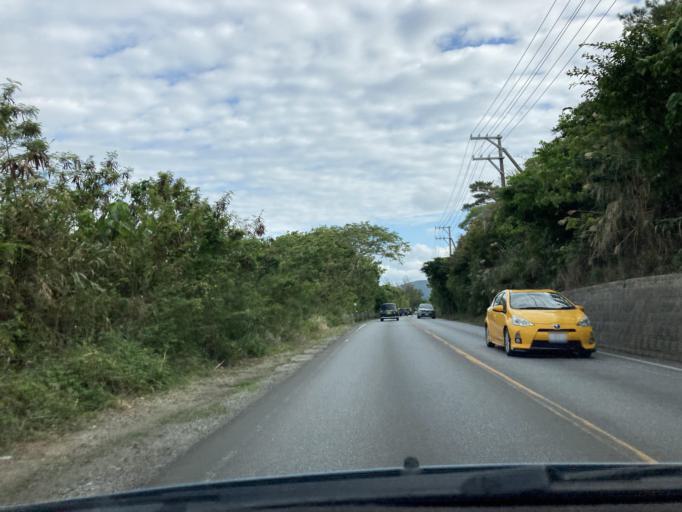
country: JP
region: Okinawa
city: Nago
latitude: 26.6431
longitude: 127.9984
